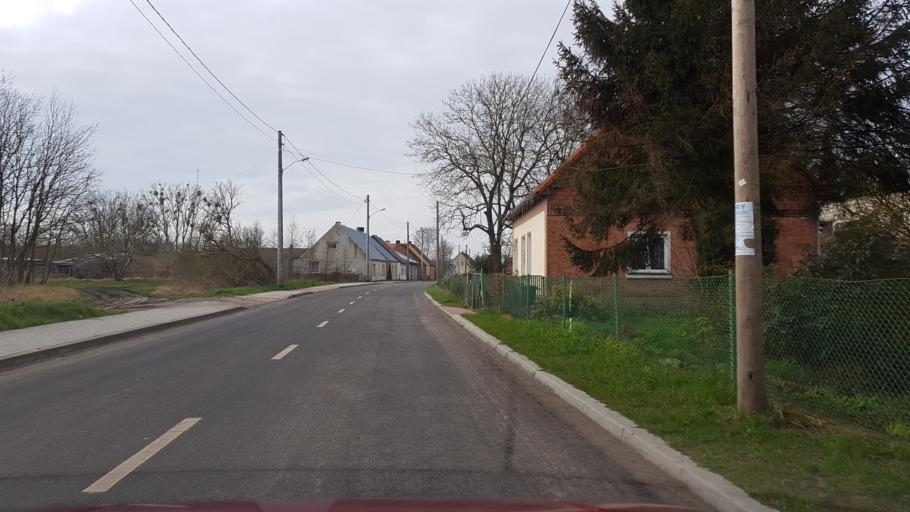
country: PL
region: West Pomeranian Voivodeship
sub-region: Powiat policki
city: Nowe Warpno
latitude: 53.6951
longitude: 14.3585
